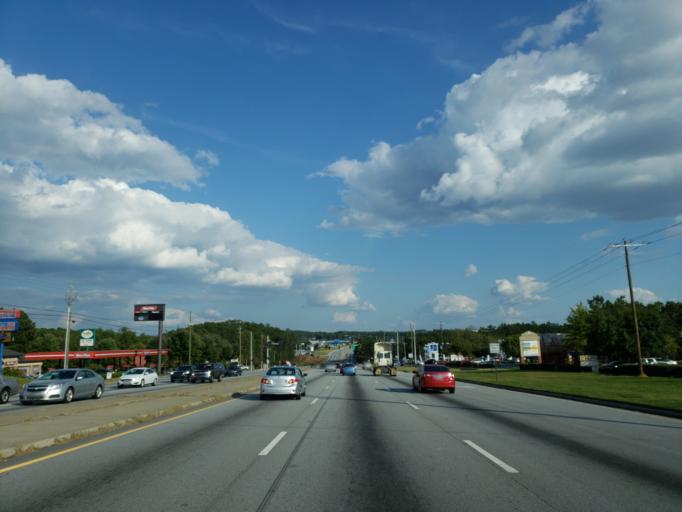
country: US
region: Georgia
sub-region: Cobb County
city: Austell
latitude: 33.7877
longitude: -84.6196
